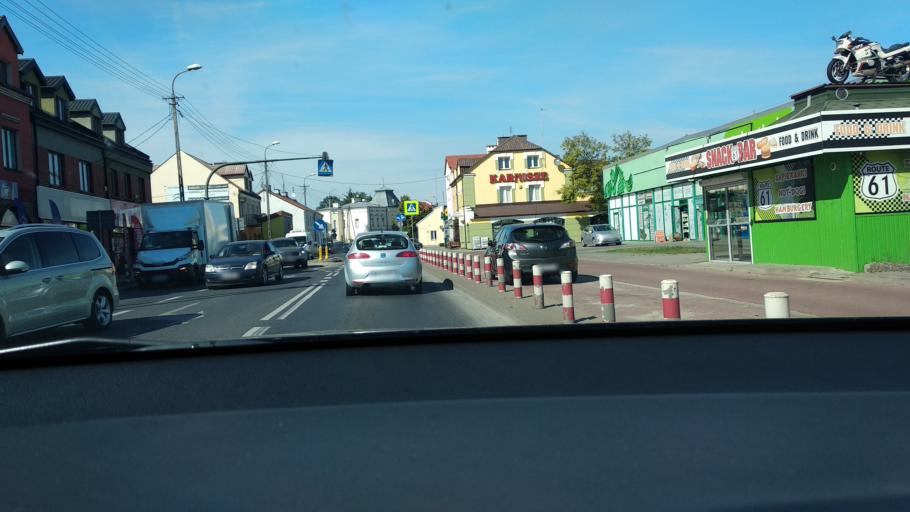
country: PL
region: Masovian Voivodeship
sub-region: Powiat pultuski
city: Pultusk
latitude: 52.7013
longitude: 21.0855
